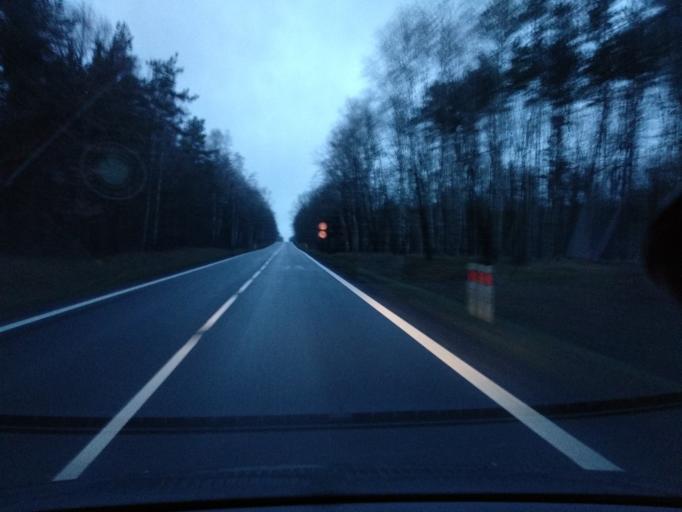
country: PL
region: Lower Silesian Voivodeship
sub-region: Powiat legnicki
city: Prochowice
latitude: 51.2468
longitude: 16.4074
